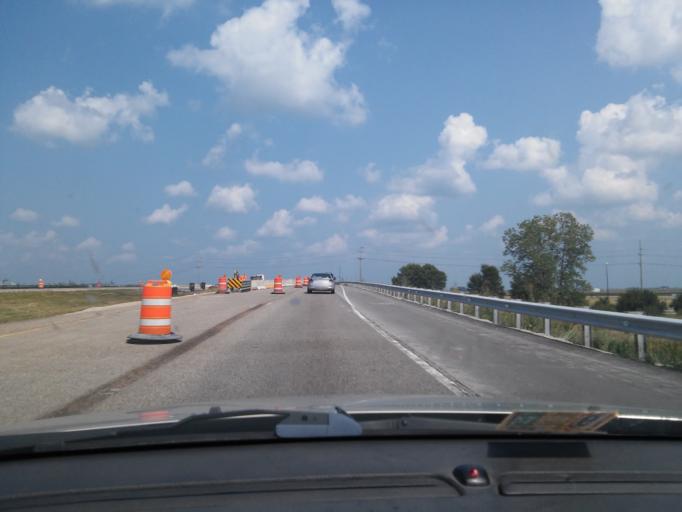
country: US
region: Illinois
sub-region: Logan County
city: Lincoln
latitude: 40.1851
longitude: -89.3231
